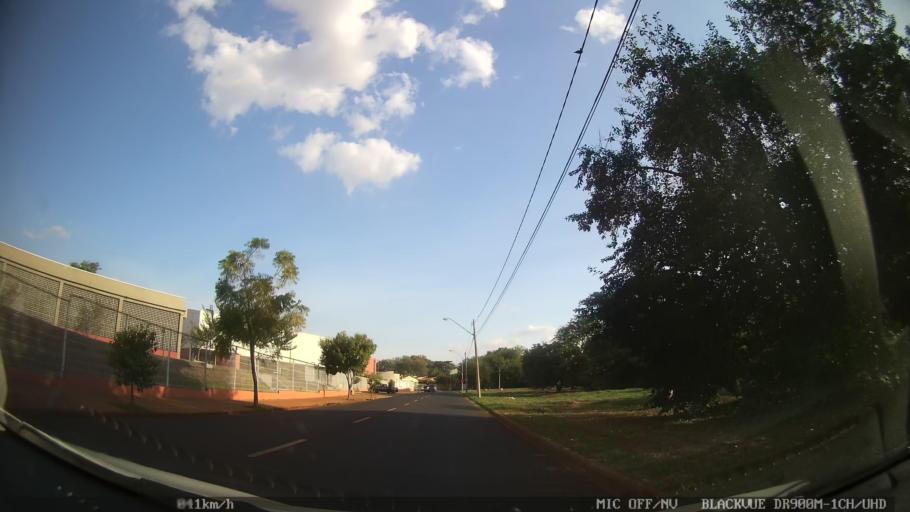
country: BR
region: Sao Paulo
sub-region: Ribeirao Preto
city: Ribeirao Preto
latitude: -21.1470
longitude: -47.8362
